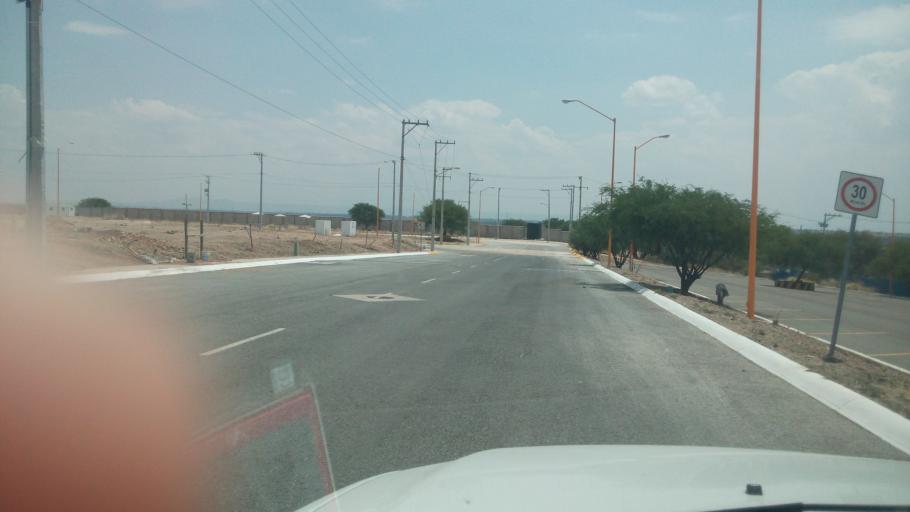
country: MX
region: Aguascalientes
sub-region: Aguascalientes
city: Villa Licenciado Jesus Teran (Calvillito)
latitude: 21.8669
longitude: -102.1772
